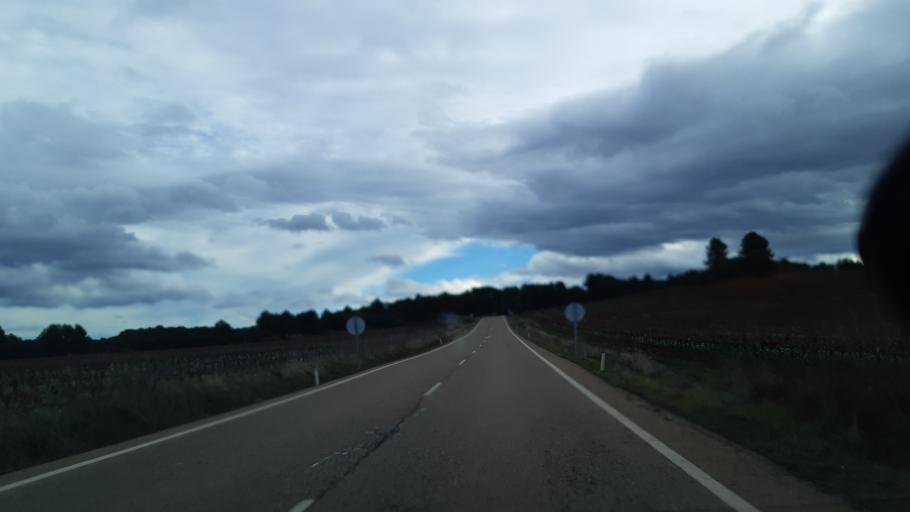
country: ES
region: Aragon
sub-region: Provincia de Teruel
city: Calaceite
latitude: 40.9610
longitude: 0.2132
